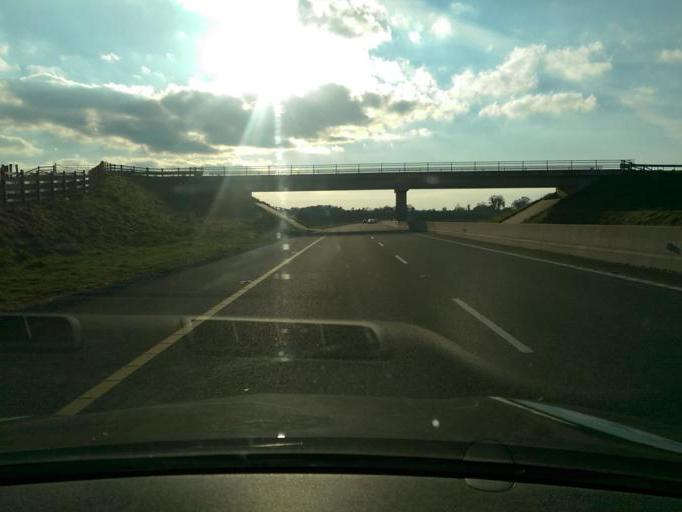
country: IE
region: Munster
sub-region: North Tipperary
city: Roscrea
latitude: 52.9152
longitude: -7.6941
